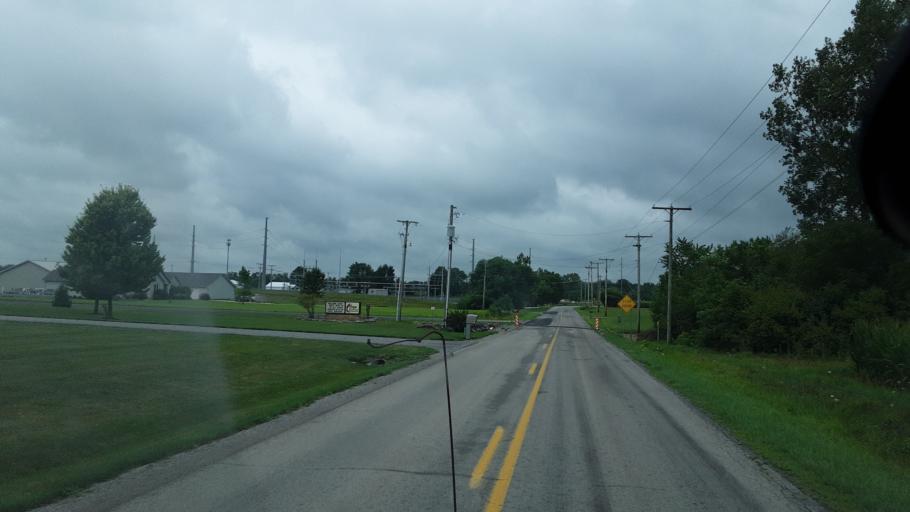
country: US
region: Indiana
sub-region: Allen County
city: New Haven
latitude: 40.9469
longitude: -85.0506
